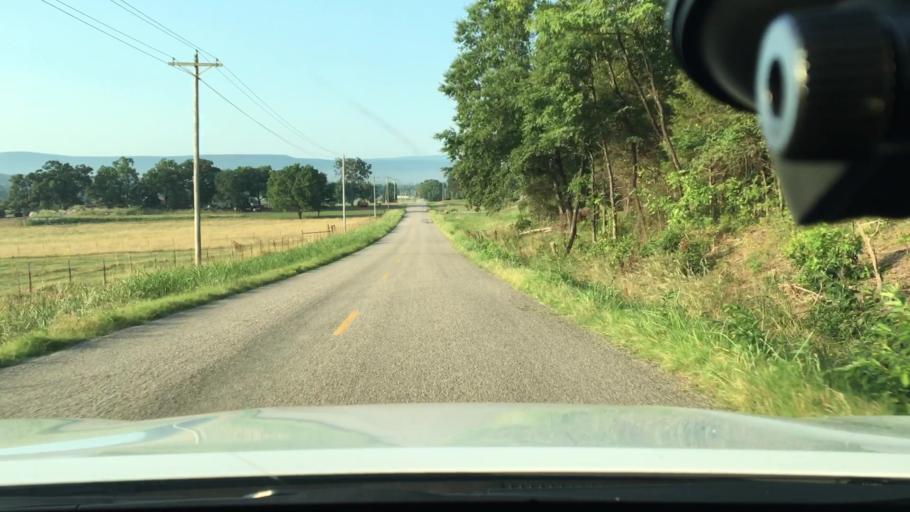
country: US
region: Arkansas
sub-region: Johnson County
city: Coal Hill
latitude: 35.3488
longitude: -93.6134
